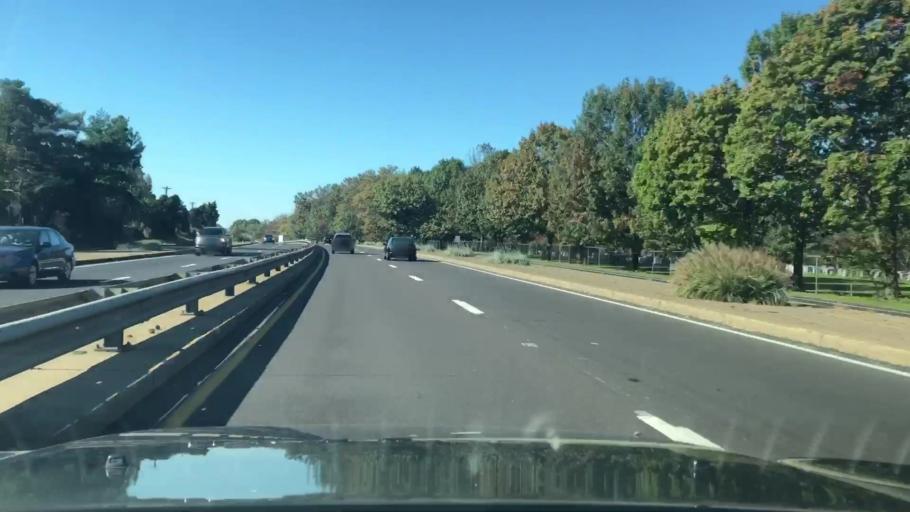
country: US
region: Pennsylvania
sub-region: Bucks County
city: Langhorne
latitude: 40.1643
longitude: -74.9316
